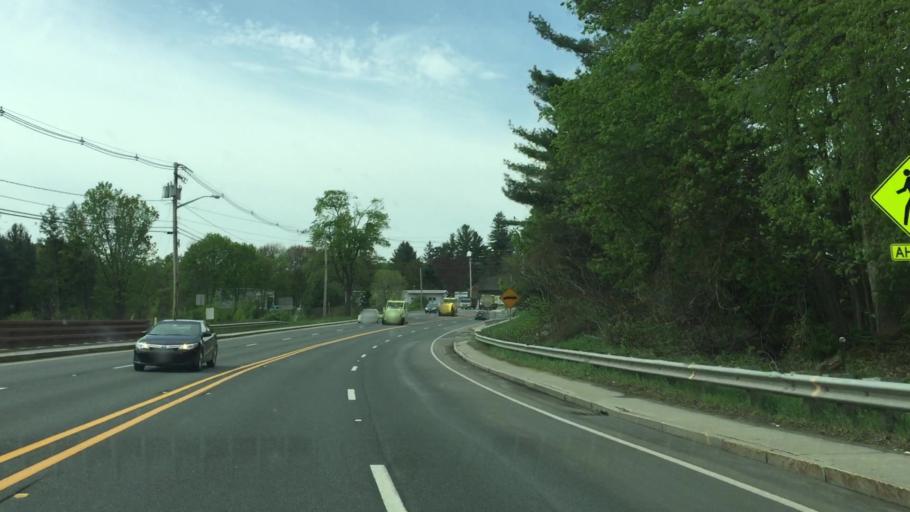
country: US
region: Massachusetts
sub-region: Berkshire County
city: Lenox
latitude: 42.3999
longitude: -73.2672
